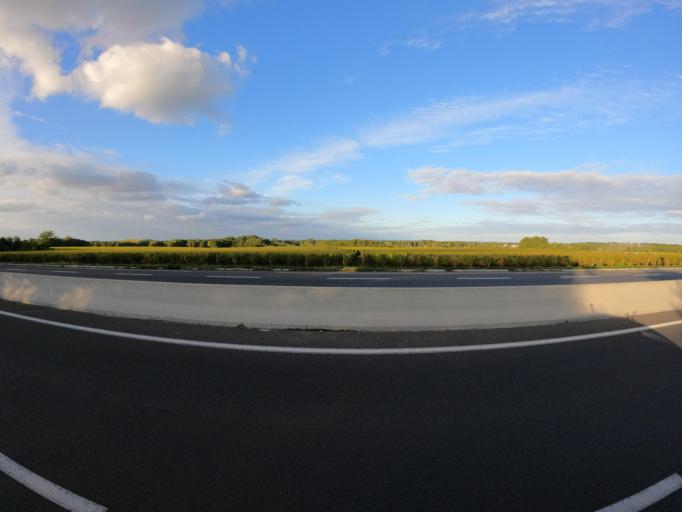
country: FR
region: Pays de la Loire
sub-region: Departement de Maine-et-Loire
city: Saint-Melaine-sur-Aubance
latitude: 47.3859
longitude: -0.4875
